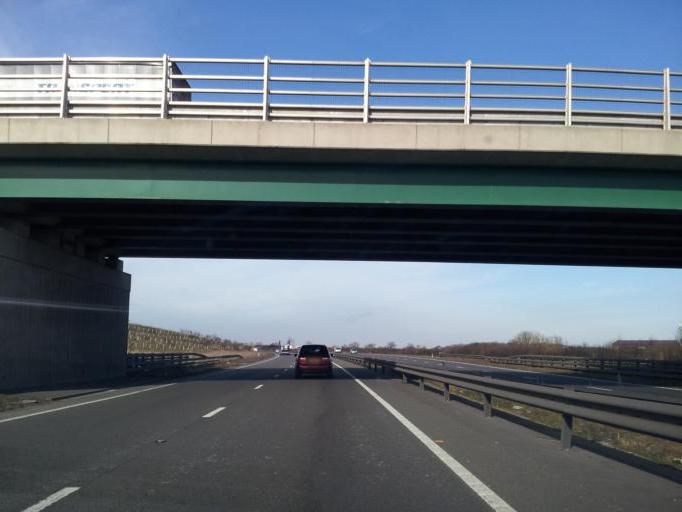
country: GB
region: England
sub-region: Lincolnshire
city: Great Gonerby
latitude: 52.9501
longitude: -0.6825
